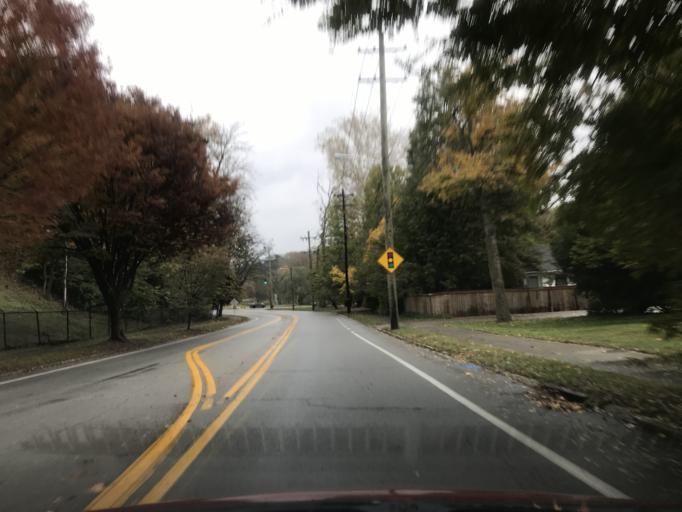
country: US
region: Kentucky
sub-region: Jefferson County
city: Audubon Park
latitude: 38.2429
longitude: -85.7070
